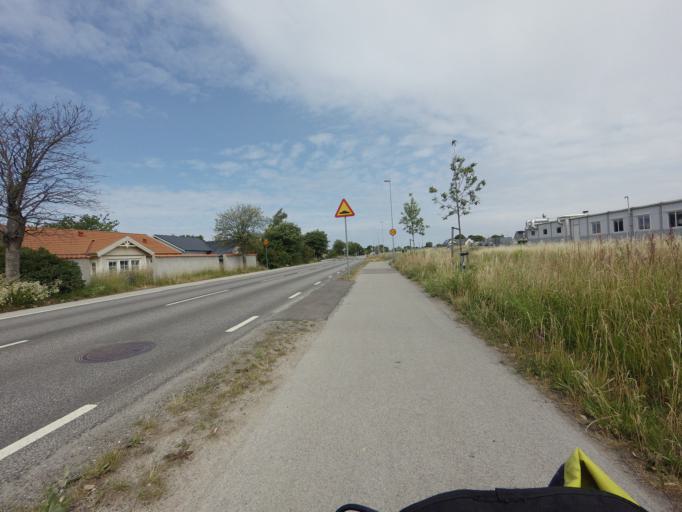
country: SE
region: Skane
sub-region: Malmo
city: Bunkeflostrand
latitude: 55.5400
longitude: 12.9196
